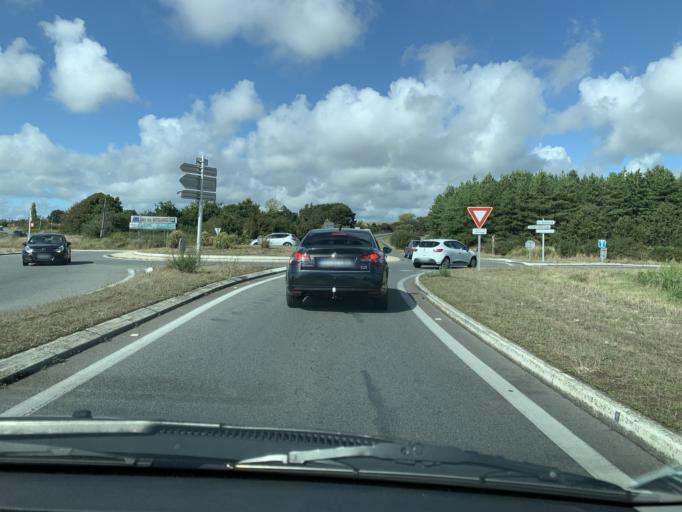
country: FR
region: Pays de la Loire
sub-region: Departement de la Loire-Atlantique
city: Guerande
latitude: 47.3145
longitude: -2.4287
